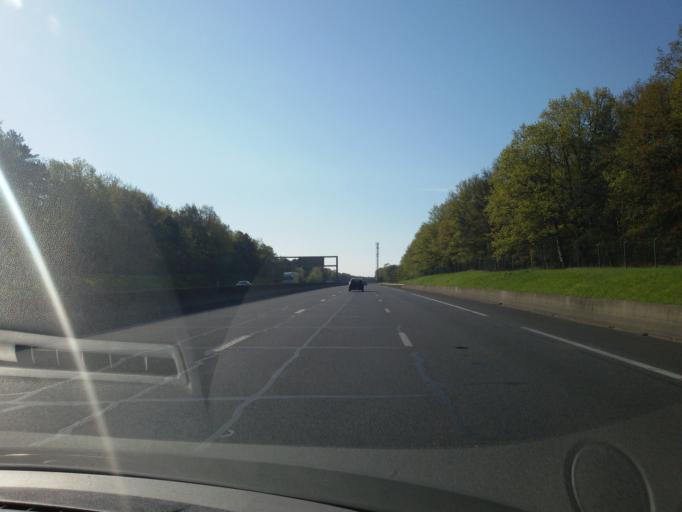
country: FR
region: Ile-de-France
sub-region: Departement de Seine-et-Marne
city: Bagneaux-sur-Loing
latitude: 48.2515
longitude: 2.7344
